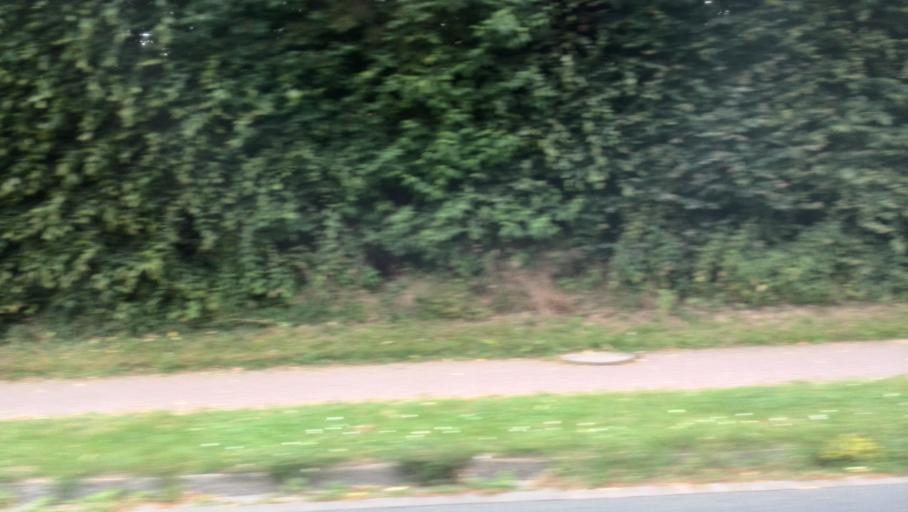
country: DE
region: Lower Saxony
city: Holle
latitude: 52.0931
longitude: 10.1550
